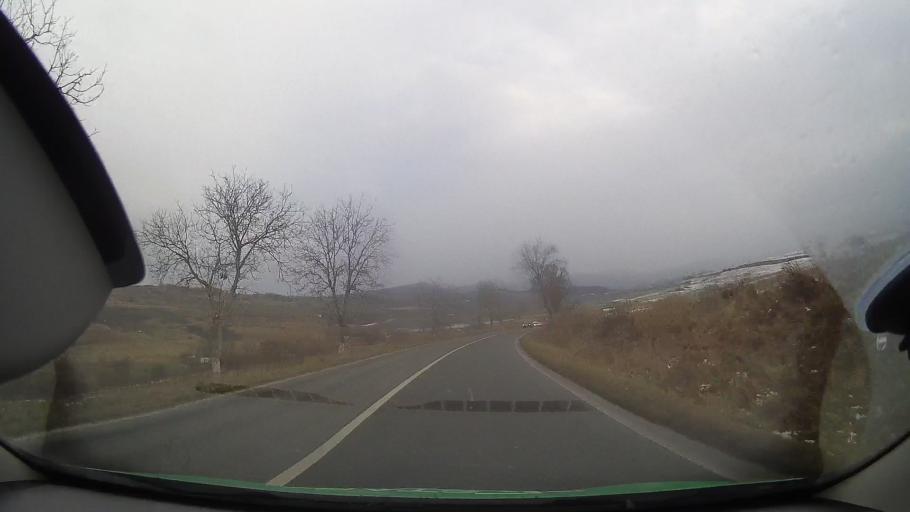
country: RO
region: Sibiu
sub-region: Comuna Blajel
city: Blajel
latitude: 46.2391
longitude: 24.3031
